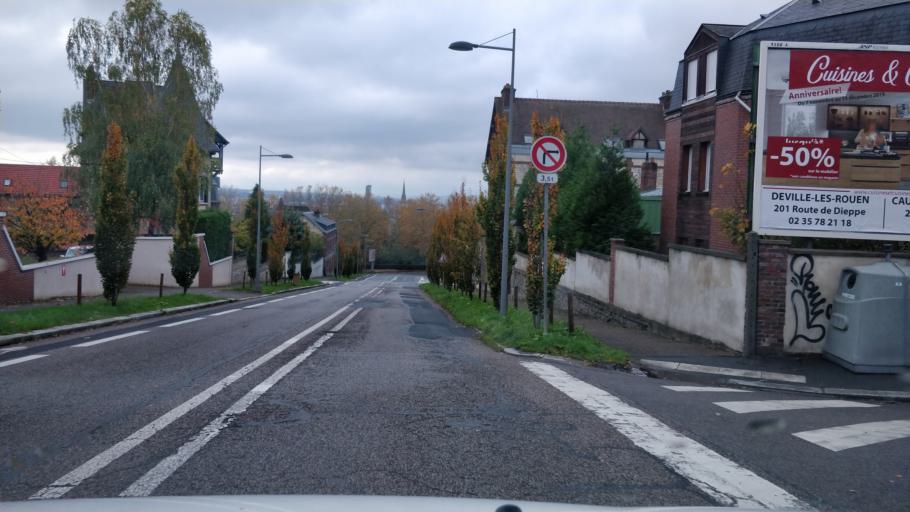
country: FR
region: Haute-Normandie
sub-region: Departement de la Seine-Maritime
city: Rouen
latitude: 49.4471
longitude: 1.1102
